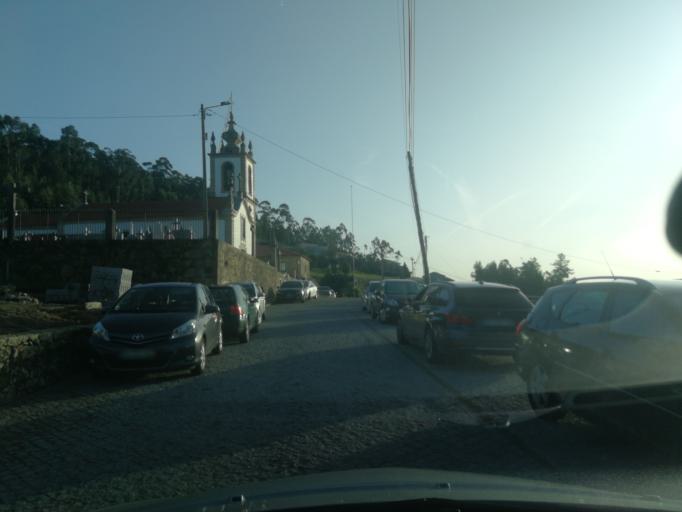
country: PT
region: Braga
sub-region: Barcelos
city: Galegos
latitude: 41.5161
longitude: -8.5586
